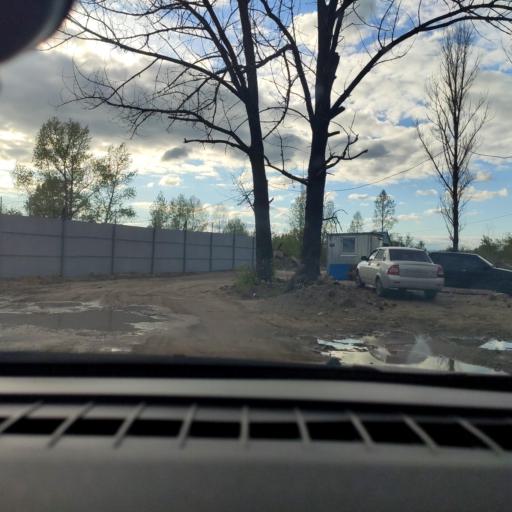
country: RU
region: Voronezj
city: Somovo
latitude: 51.7239
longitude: 39.2853
